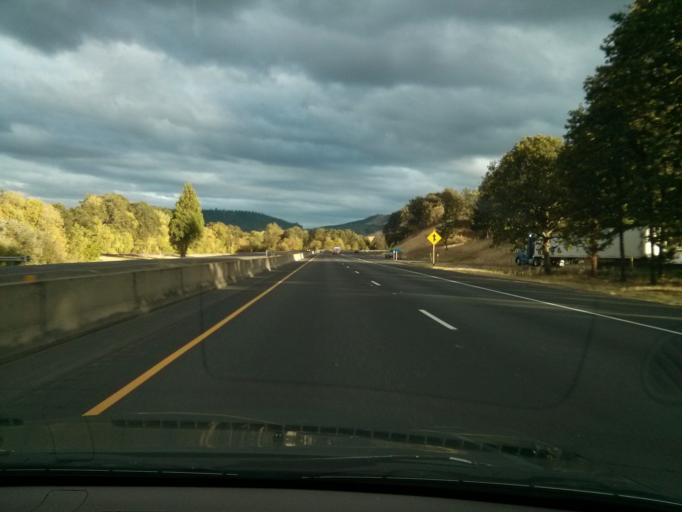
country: US
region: Oregon
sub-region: Douglas County
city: Sutherlin
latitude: 43.4765
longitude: -123.3196
